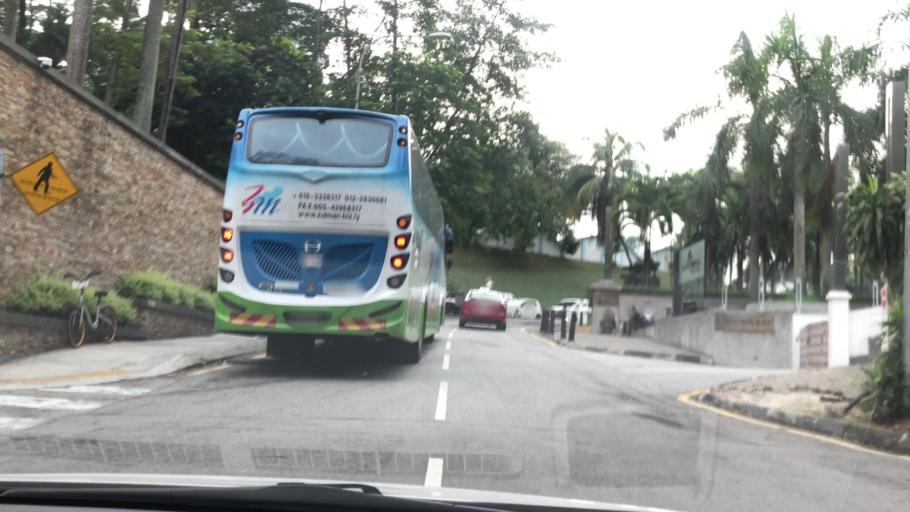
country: MY
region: Kuala Lumpur
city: Kuala Lumpur
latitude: 3.1524
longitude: 101.7054
